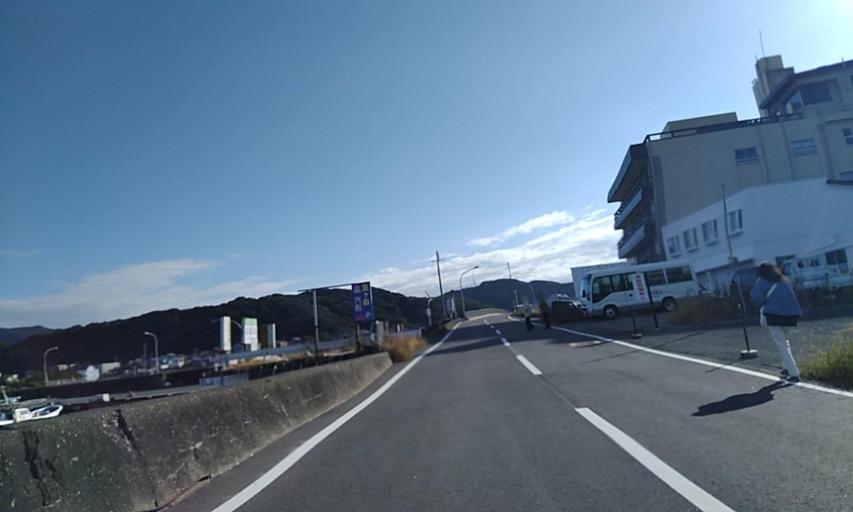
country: JP
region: Wakayama
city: Minato
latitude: 34.2754
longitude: 135.0689
